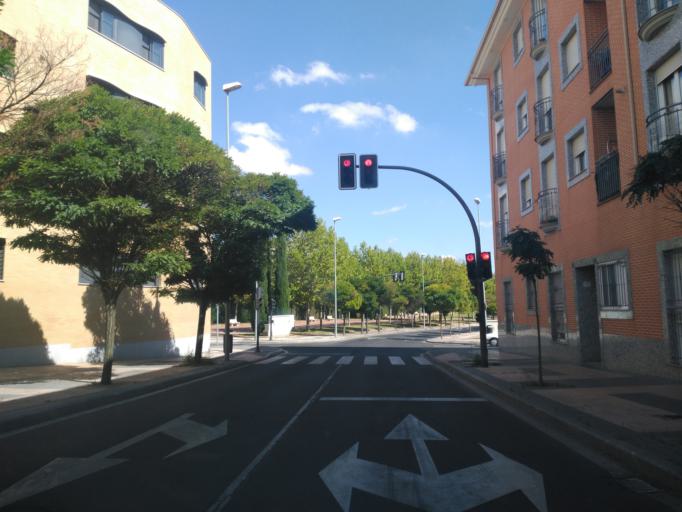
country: ES
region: Castille and Leon
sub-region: Provincia de Salamanca
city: Cabrerizos
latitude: 40.9744
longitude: -5.6319
